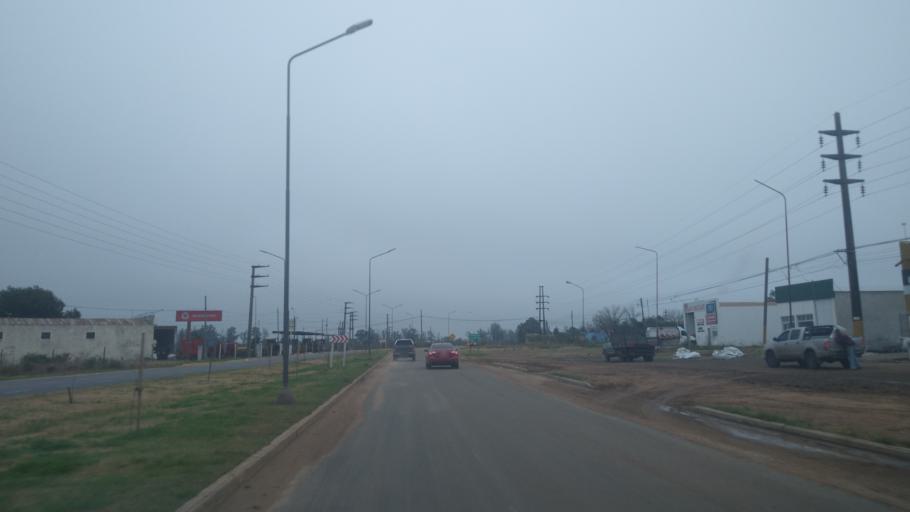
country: AR
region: Entre Rios
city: Chajari
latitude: -30.7622
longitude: -58.0127
